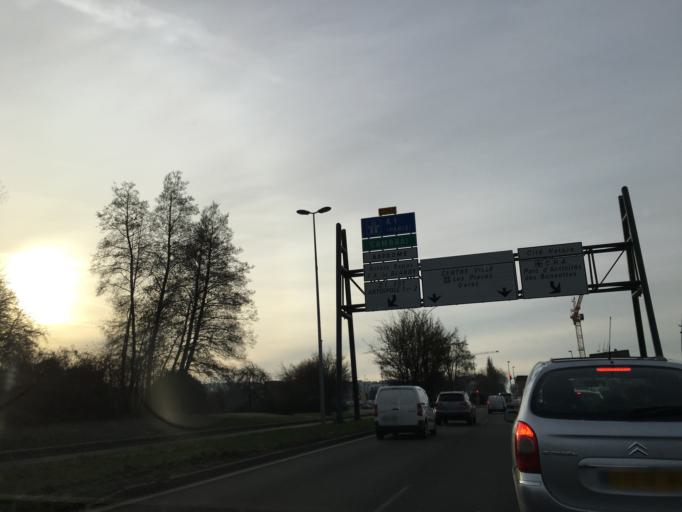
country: FR
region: Nord-Pas-de-Calais
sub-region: Departement du Pas-de-Calais
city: Arras
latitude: 50.2982
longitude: 2.7835
